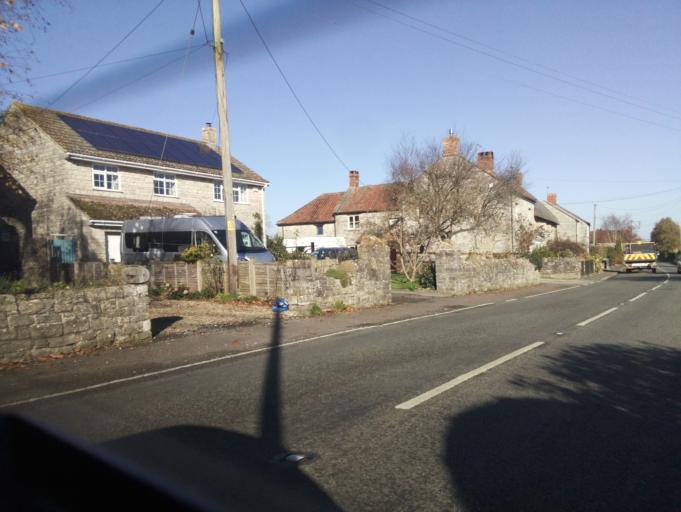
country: GB
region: England
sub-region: Somerset
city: Martock
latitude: 51.0067
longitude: -2.7626
